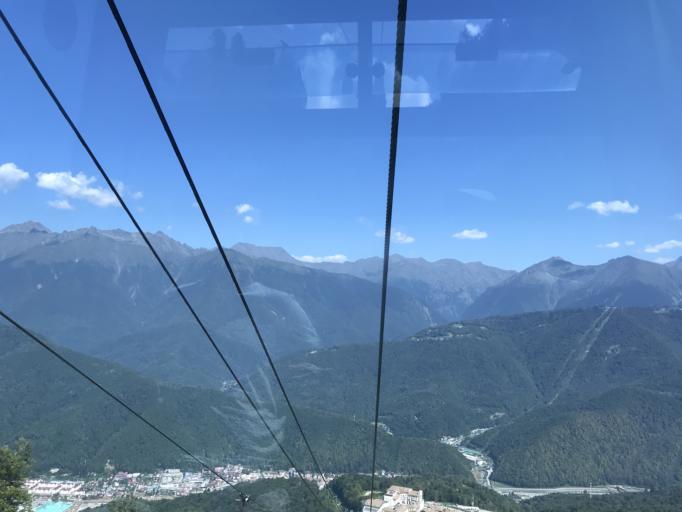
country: RU
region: Krasnodarskiy
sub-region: Sochi City
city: Krasnaya Polyana
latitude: 43.6618
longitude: 40.2531
